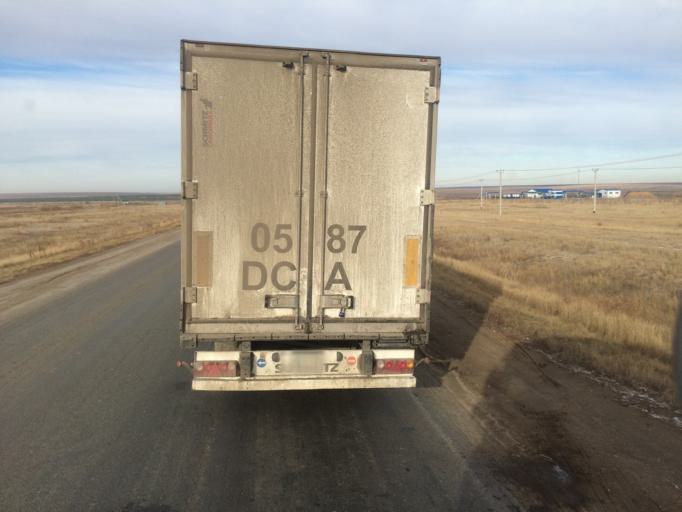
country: KZ
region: Batys Qazaqstan
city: Peremetnoe
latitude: 51.6601
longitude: 51.0084
